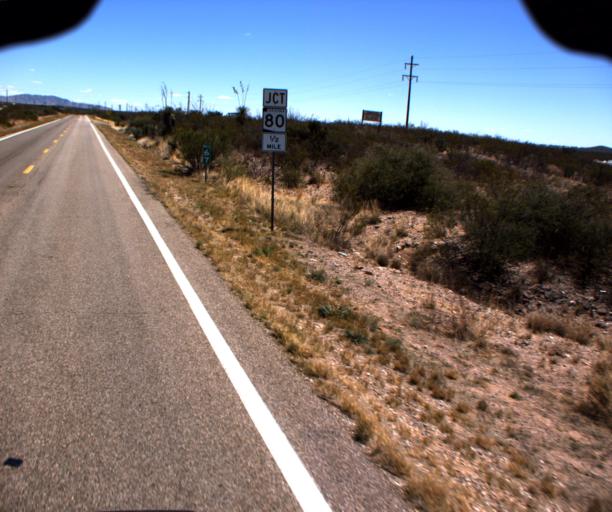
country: US
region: Arizona
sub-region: Cochise County
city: Tombstone
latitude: 31.7482
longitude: -110.1055
